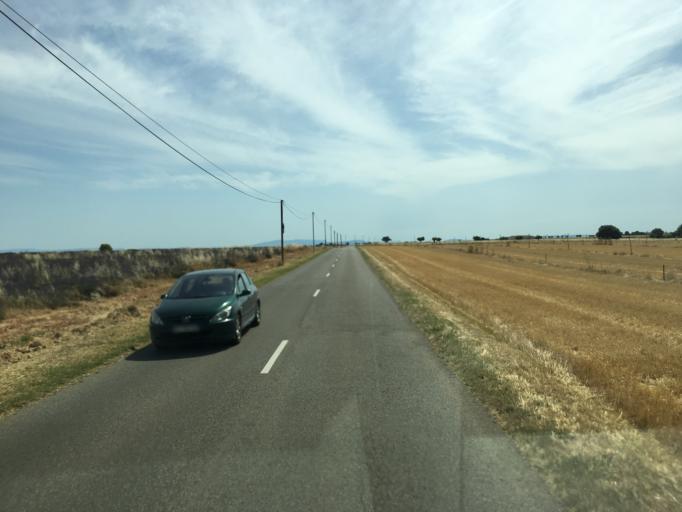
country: FR
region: Provence-Alpes-Cote d'Azur
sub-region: Departement des Alpes-de-Haute-Provence
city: Valensole
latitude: 43.8723
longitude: 6.0204
